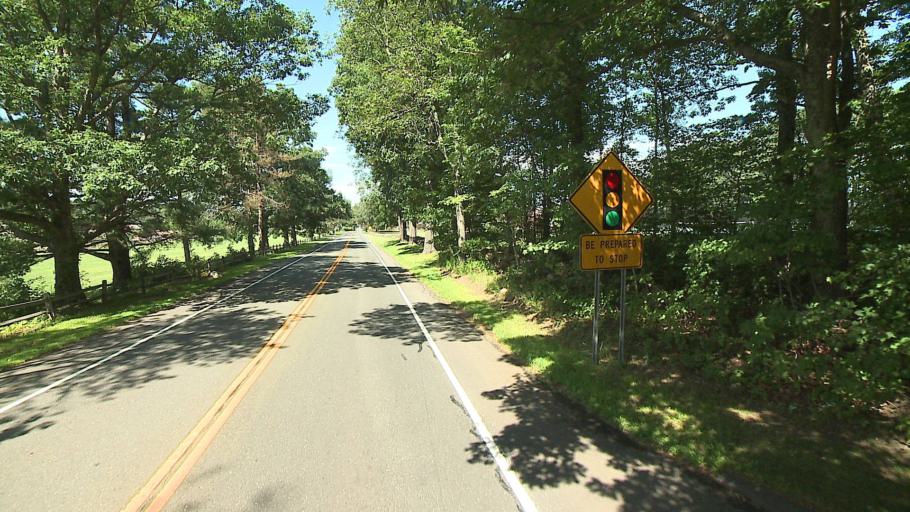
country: US
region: Connecticut
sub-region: Hartford County
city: Weatogue
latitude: 41.8470
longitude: -72.8364
